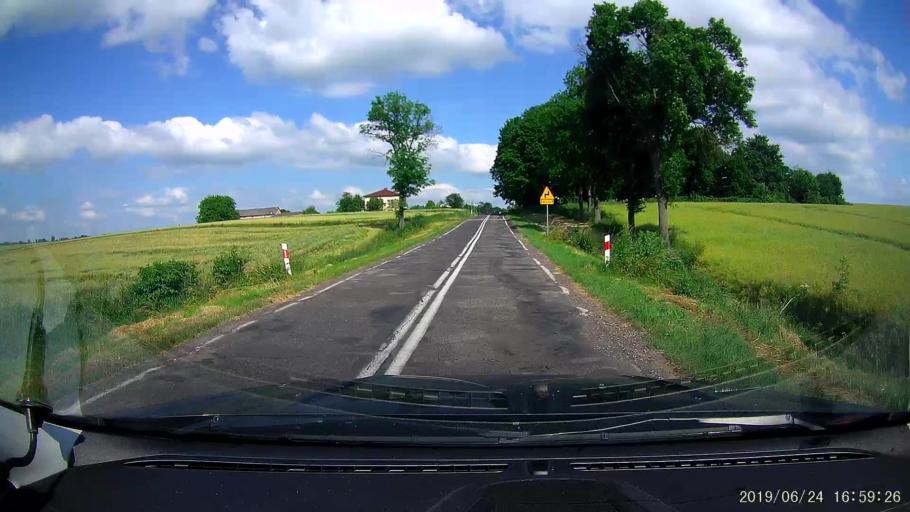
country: PL
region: Lublin Voivodeship
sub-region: Powiat tomaszowski
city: Telatyn
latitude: 50.5235
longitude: 23.9023
